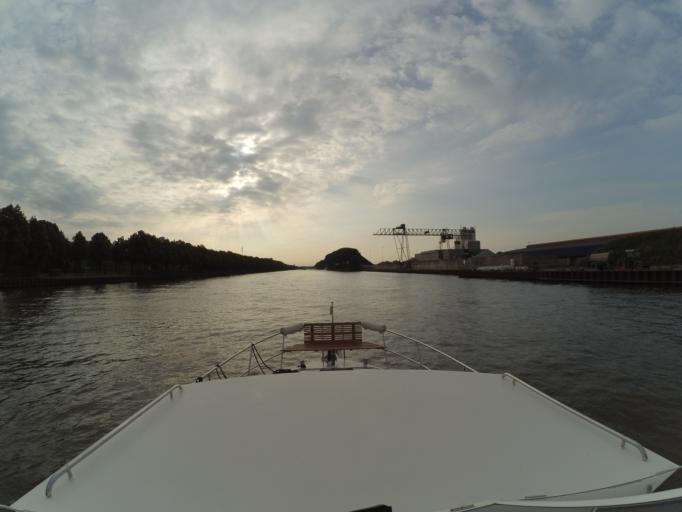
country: NL
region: Utrecht
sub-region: Stichtse Vecht
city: Maarssen
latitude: 52.1244
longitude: 5.0577
